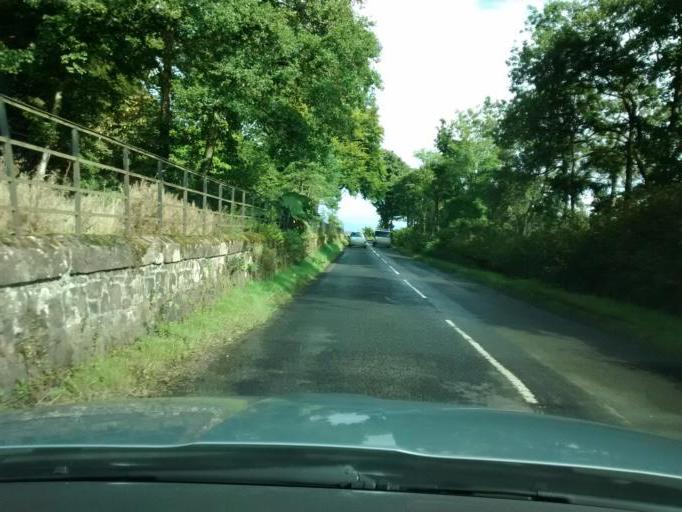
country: GB
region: Scotland
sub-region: North Ayrshire
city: Lamlash
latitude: 55.5926
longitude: -5.1483
